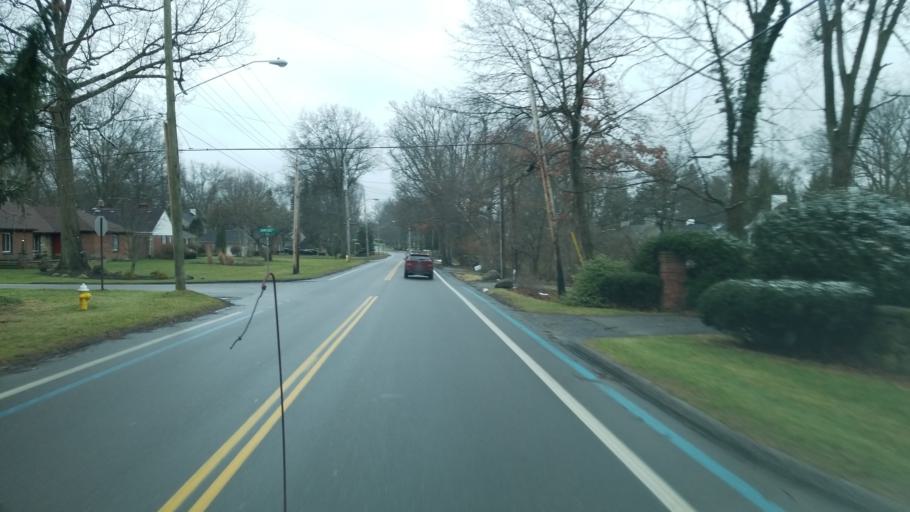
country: US
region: Ohio
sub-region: Summit County
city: Akron
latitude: 41.1125
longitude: -81.5486
